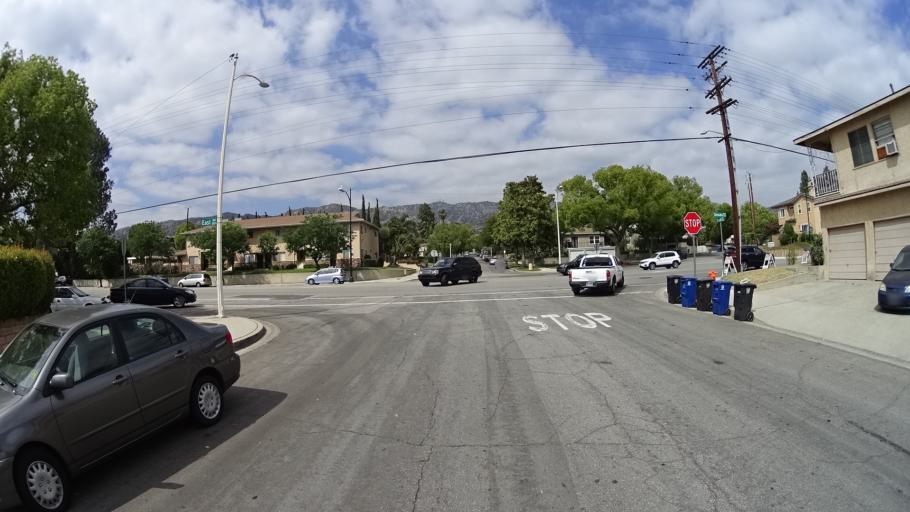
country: US
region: California
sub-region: Los Angeles County
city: Burbank
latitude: 34.1907
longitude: -118.3171
